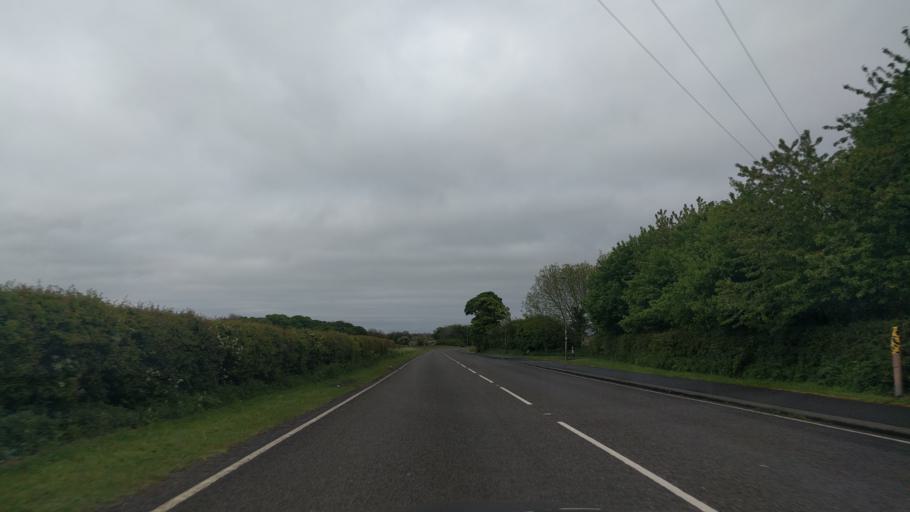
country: GB
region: England
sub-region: Northumberland
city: Choppington
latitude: 55.1605
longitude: -1.6216
